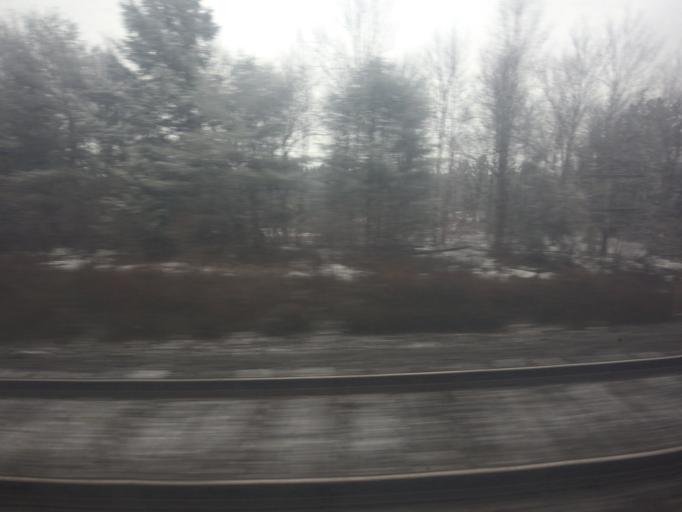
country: CA
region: Ontario
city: Brockville
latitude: 44.5517
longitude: -75.7944
